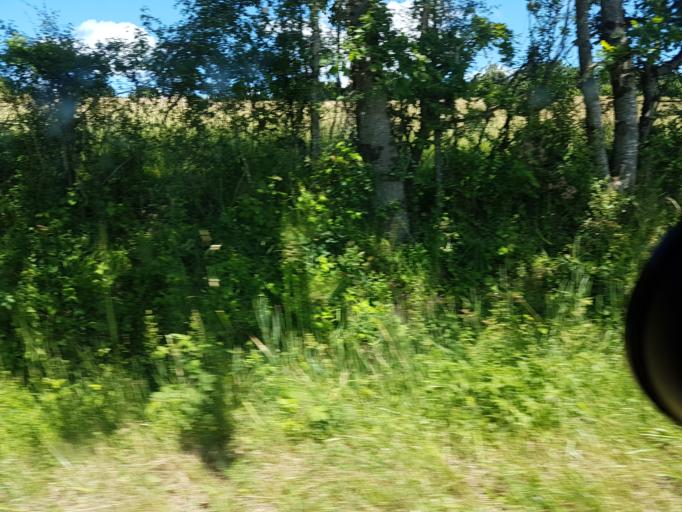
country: FR
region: Bourgogne
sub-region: Departement de Saone-et-Loire
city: Autun
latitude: 47.0564
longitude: 4.2781
